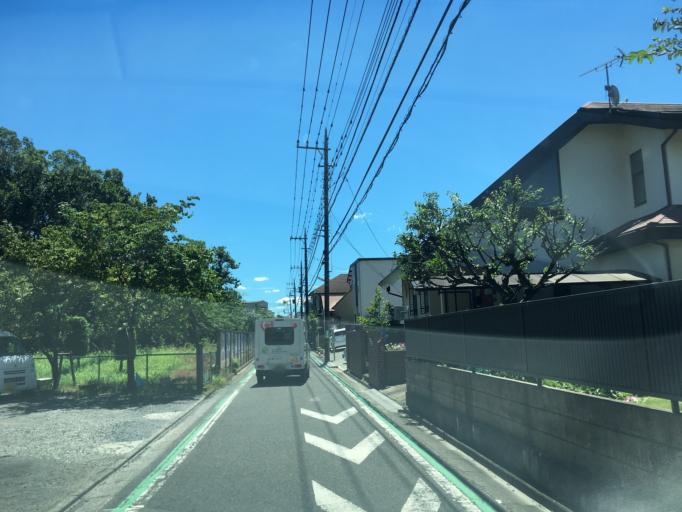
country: JP
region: Tokyo
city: Higashimurayama-shi
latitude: 35.7492
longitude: 139.4597
